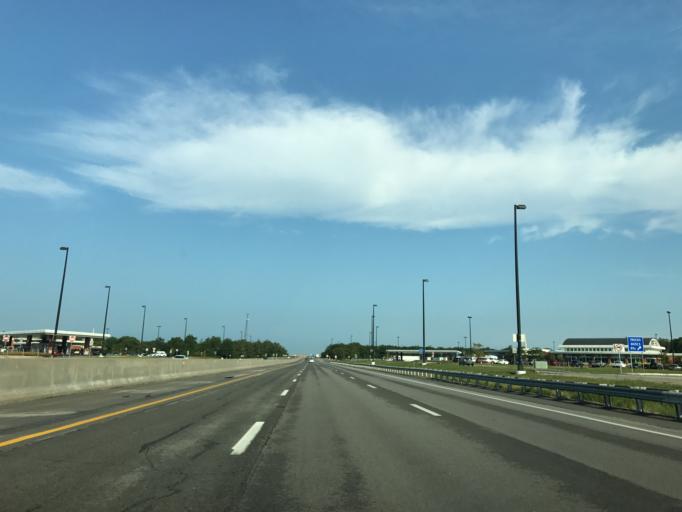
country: US
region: Ohio
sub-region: Ottawa County
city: Genoa
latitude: 41.4891
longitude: -83.3657
